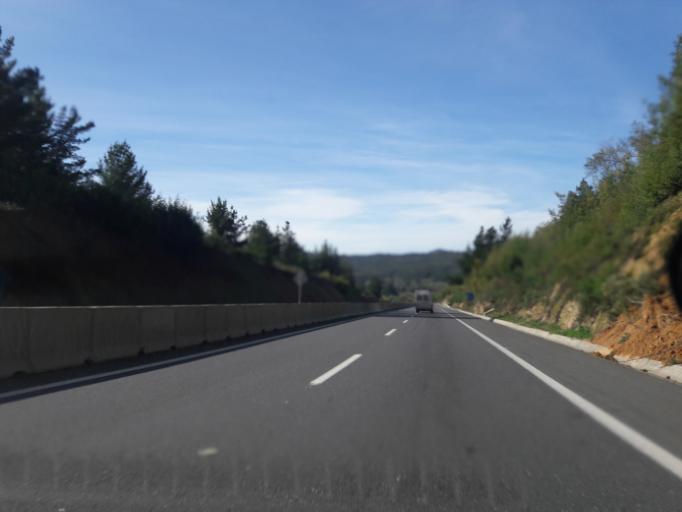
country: CL
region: Biobio
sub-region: Provincia de Biobio
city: Yumbel
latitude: -36.9780
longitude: -72.6480
